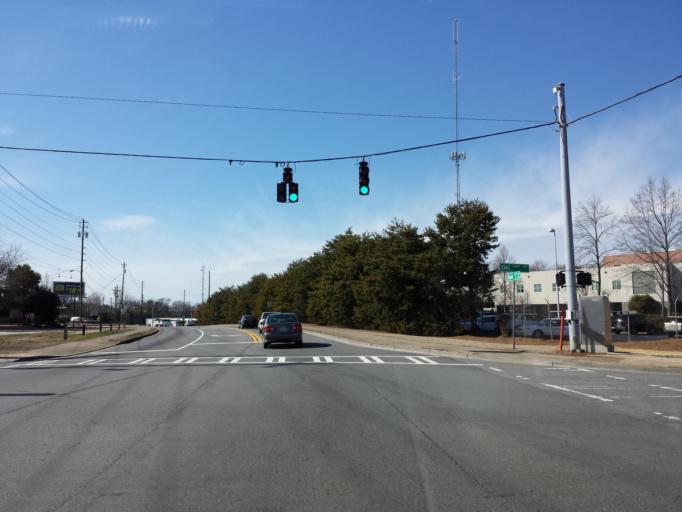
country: US
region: Georgia
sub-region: Cobb County
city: Marietta
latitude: 33.9779
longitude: -84.5559
